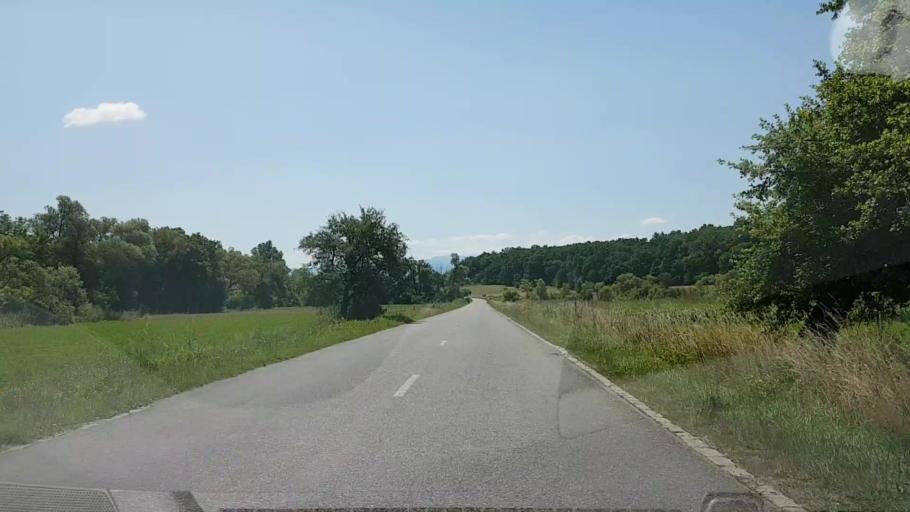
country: RO
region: Brasov
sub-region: Comuna Cincu
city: Cincu
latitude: 45.8747
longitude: 24.8193
